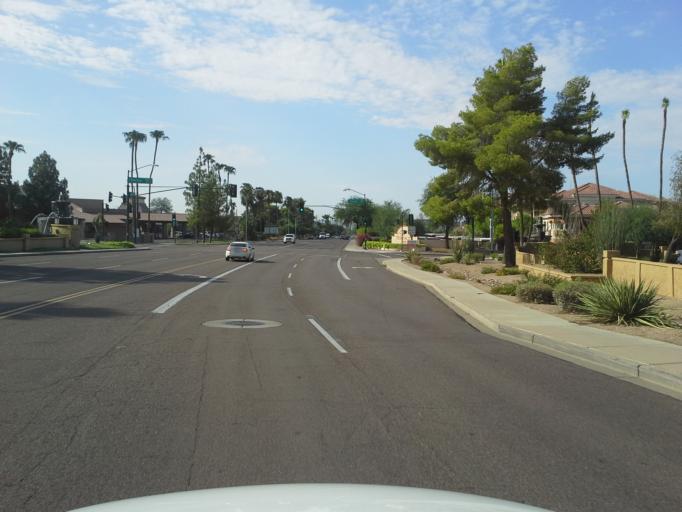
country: US
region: Arizona
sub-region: Maricopa County
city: Phoenix
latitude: 33.5482
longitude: -112.0478
